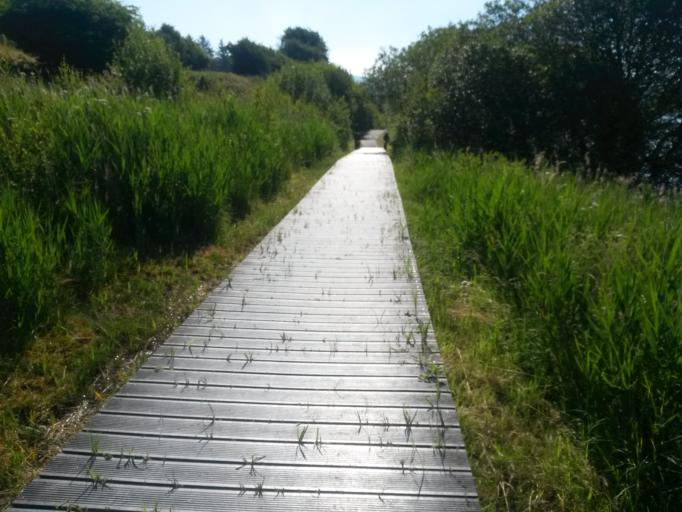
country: IE
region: Leinster
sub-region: Wicklow
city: Blessington
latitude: 53.1562
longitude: -6.5486
